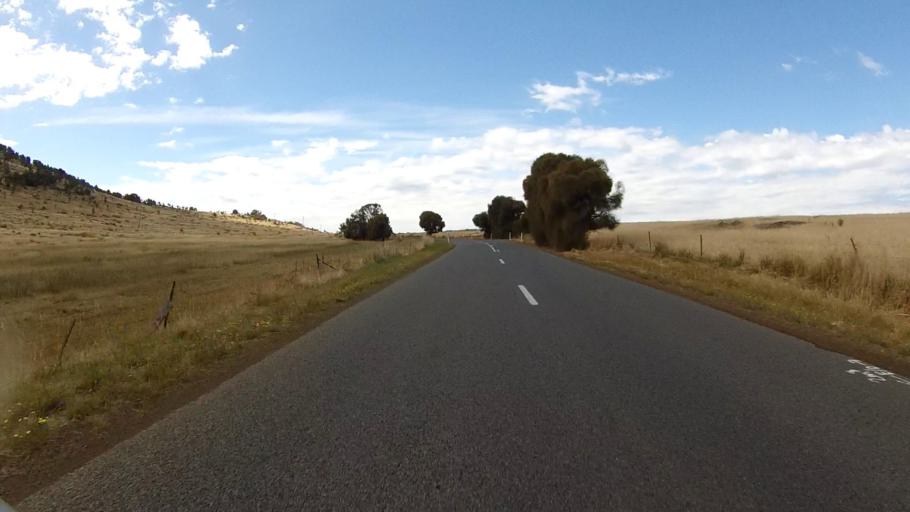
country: AU
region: Tasmania
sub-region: Sorell
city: Sorell
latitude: -42.1934
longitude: 148.0591
